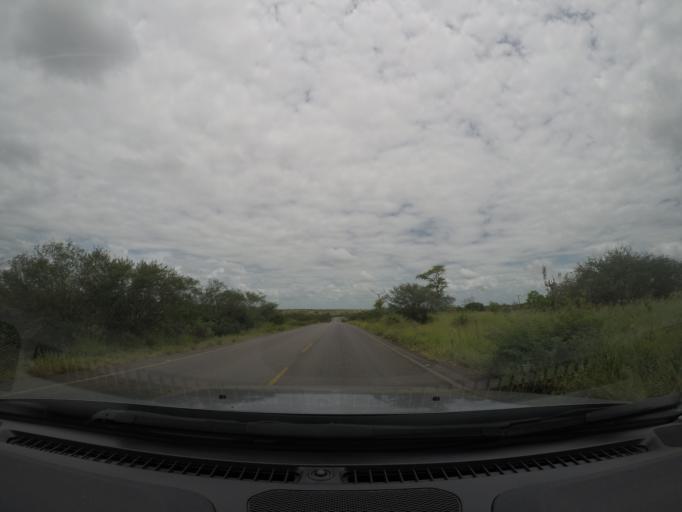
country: BR
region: Bahia
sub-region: Itaberaba
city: Itaberaba
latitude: -12.4908
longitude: -40.2333
